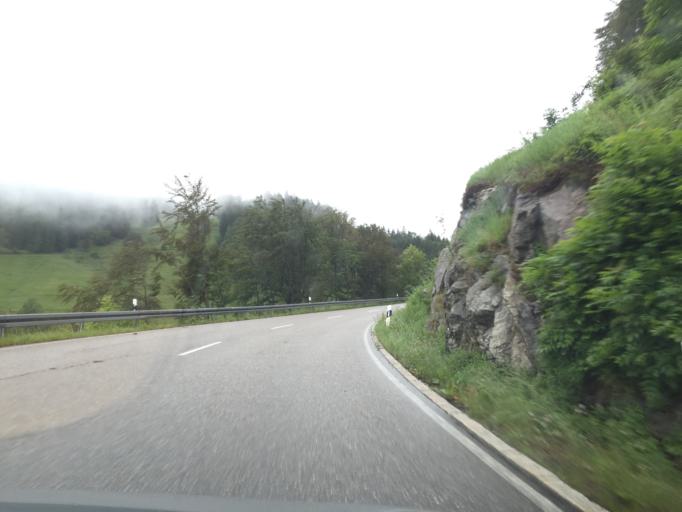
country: DE
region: Baden-Wuerttemberg
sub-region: Freiburg Region
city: Todtnau
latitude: 47.8453
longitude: 7.9262
